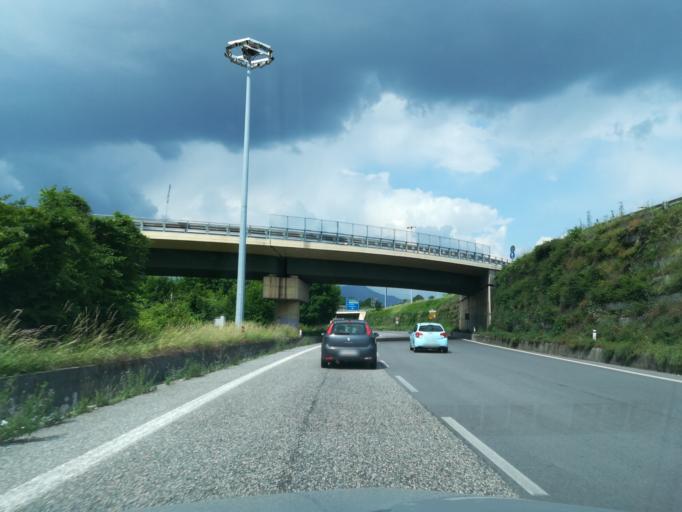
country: IT
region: Lombardy
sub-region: Provincia di Bergamo
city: Grassobbio
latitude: 45.6650
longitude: 9.7380
